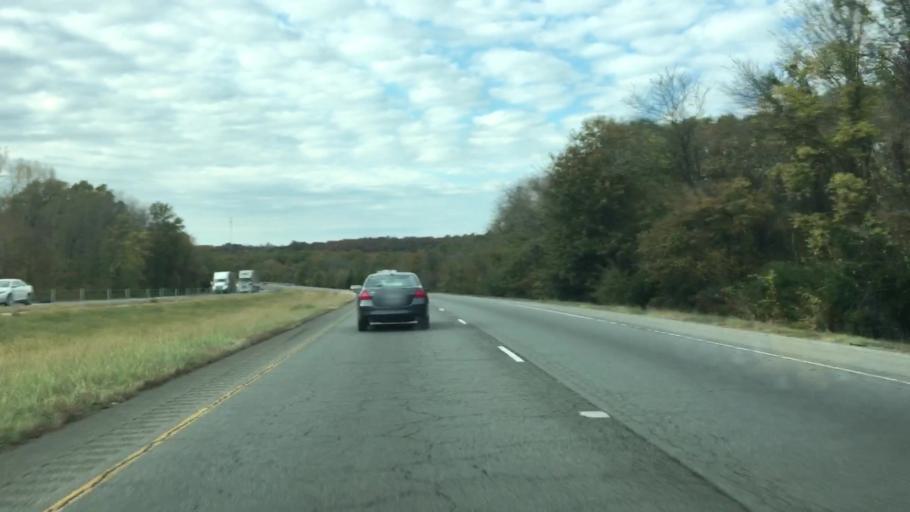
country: US
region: Arkansas
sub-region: Faulkner County
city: Conway
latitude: 35.1361
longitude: -92.5200
